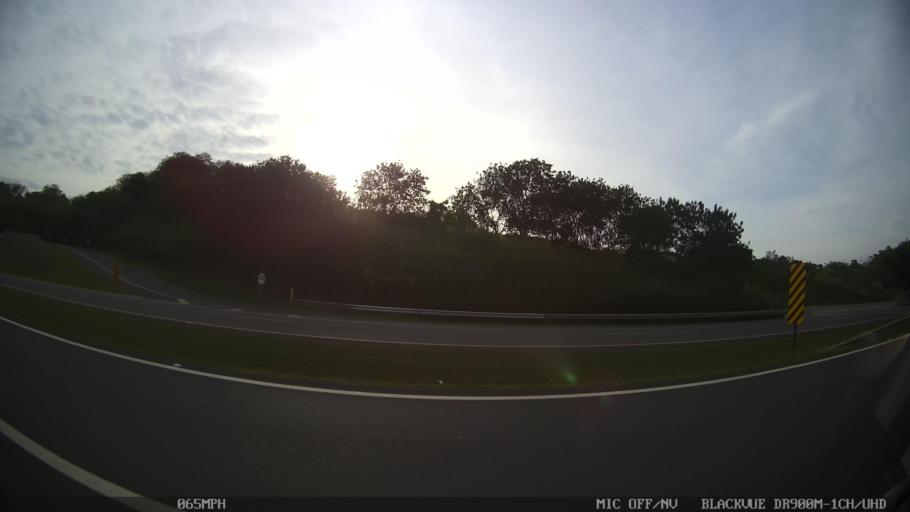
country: BR
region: Sao Paulo
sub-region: Piracicaba
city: Piracicaba
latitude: -22.6858
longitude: -47.5814
